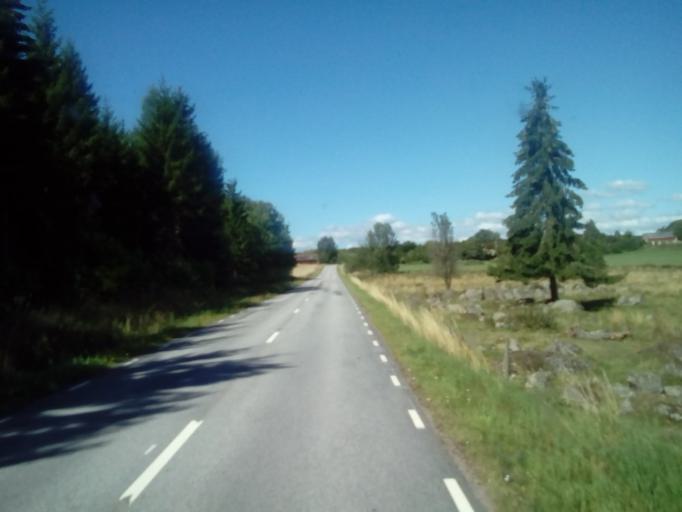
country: SE
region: Kalmar
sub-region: Vasterviks Kommun
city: Overum
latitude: 57.9014
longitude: 16.0534
